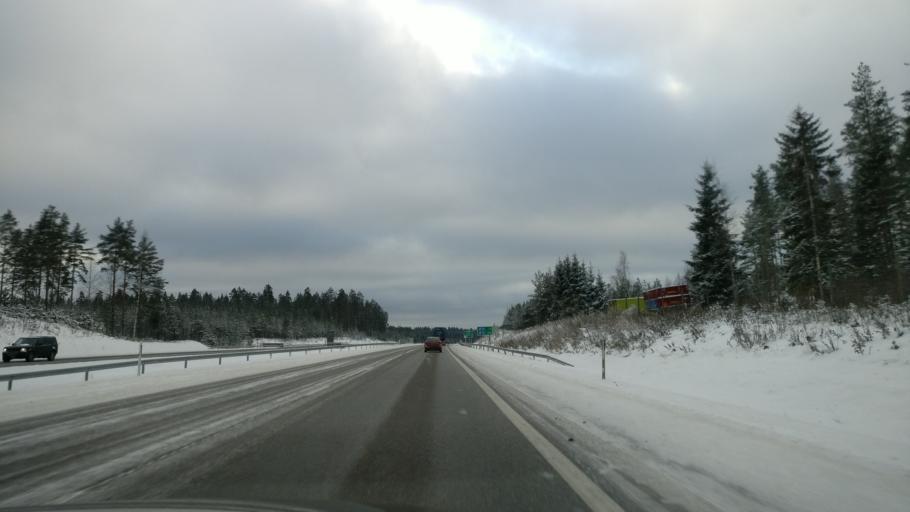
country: FI
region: Paijanne Tavastia
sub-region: Lahti
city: Heinola
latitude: 61.1075
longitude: 25.9164
